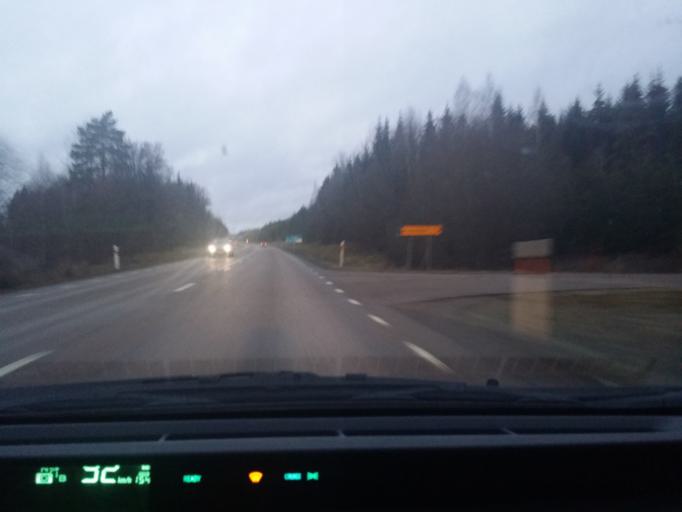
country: SE
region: Soedermanland
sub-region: Eskilstuna Kommun
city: Kvicksund
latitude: 59.4879
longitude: 16.3057
